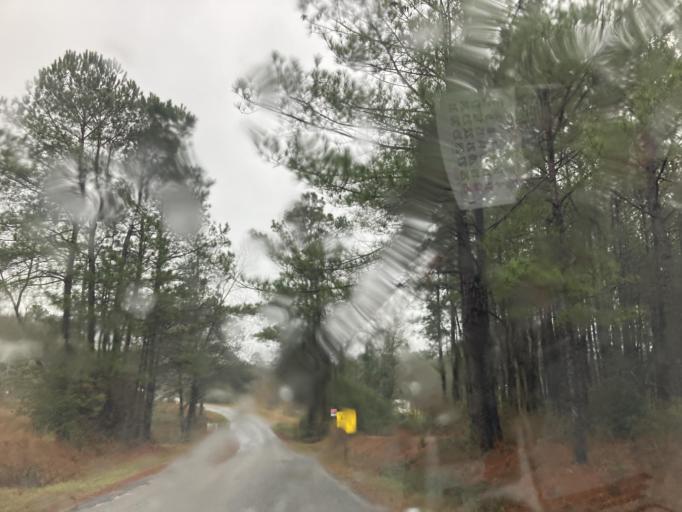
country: US
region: Mississippi
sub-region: Forrest County
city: Rawls Springs
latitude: 31.4816
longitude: -89.3861
